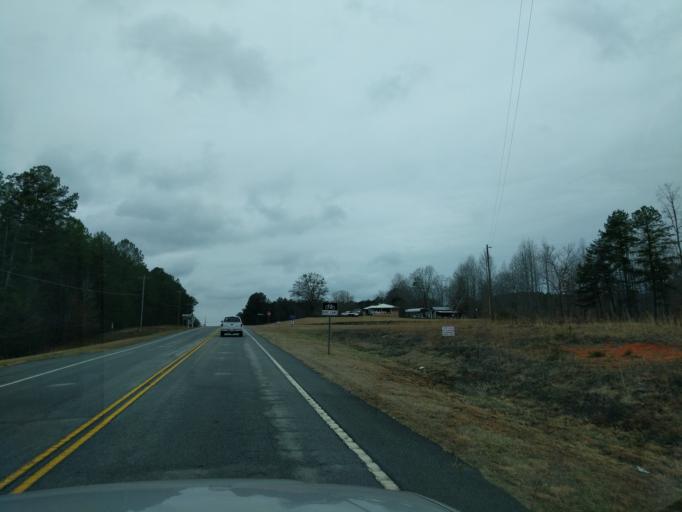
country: US
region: South Carolina
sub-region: Oconee County
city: Walhalla
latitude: 34.9101
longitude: -82.9561
